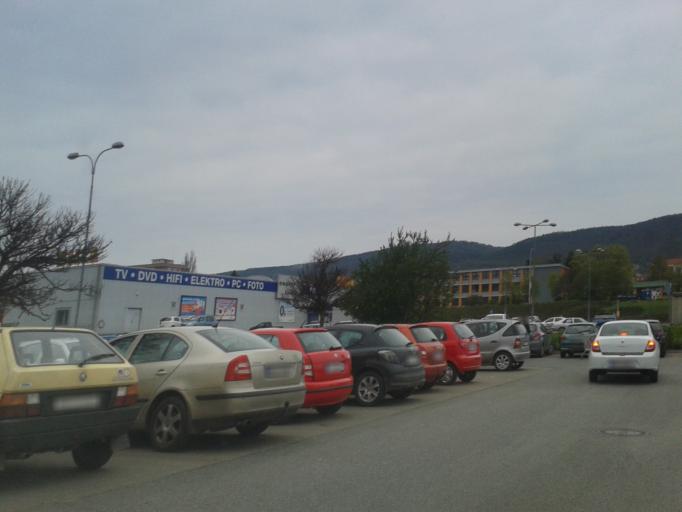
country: CZ
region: Central Bohemia
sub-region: Okres Beroun
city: Beroun
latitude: 49.9571
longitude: 14.0608
